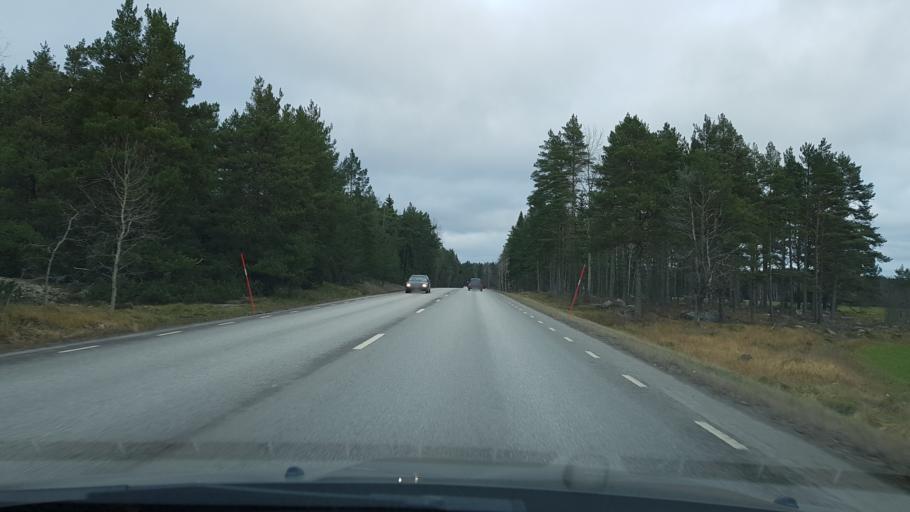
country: SE
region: Stockholm
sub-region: Norrtalje Kommun
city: Hallstavik
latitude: 60.0434
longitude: 18.5600
